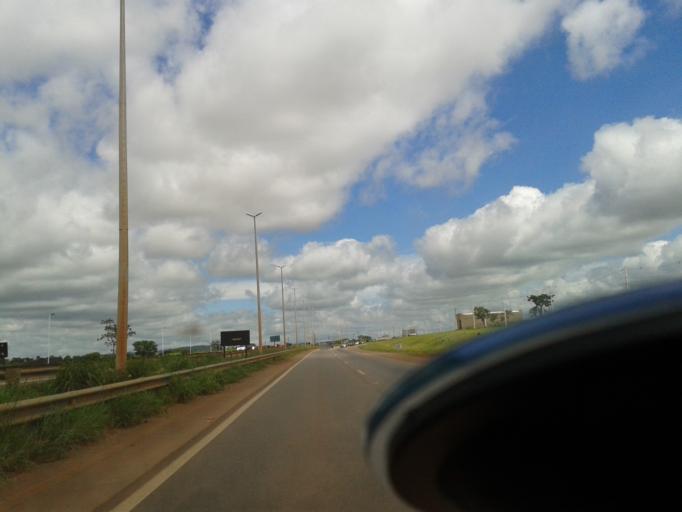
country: BR
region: Goias
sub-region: Goianira
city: Goianira
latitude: -16.5336
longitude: -49.4074
